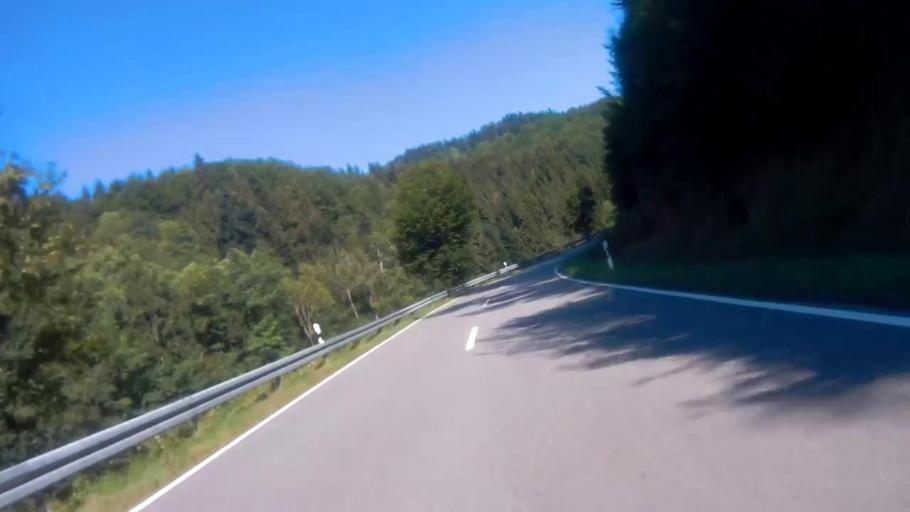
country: DE
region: Baden-Wuerttemberg
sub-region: Freiburg Region
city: Maulburg
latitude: 47.7364
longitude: 7.7654
